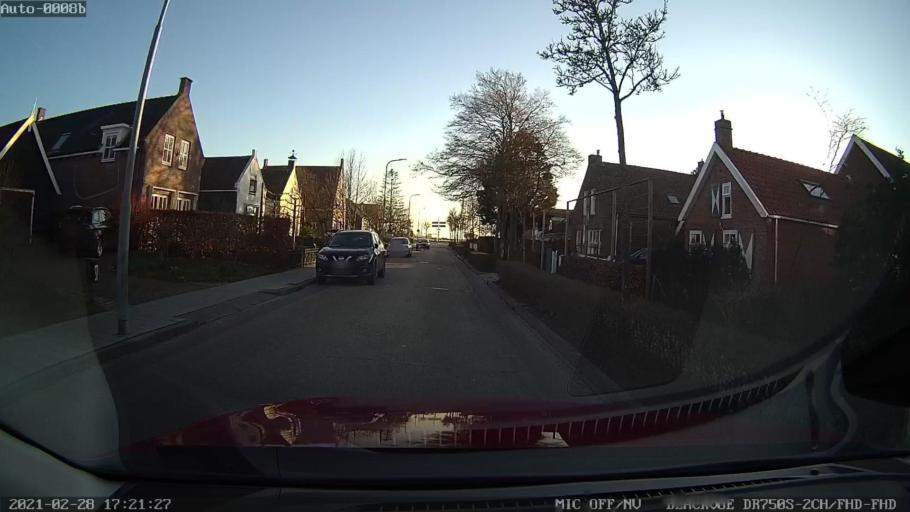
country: NL
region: Zeeland
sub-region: Schouwen-Duiveland
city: Bruinisse
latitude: 51.6843
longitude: 3.9797
